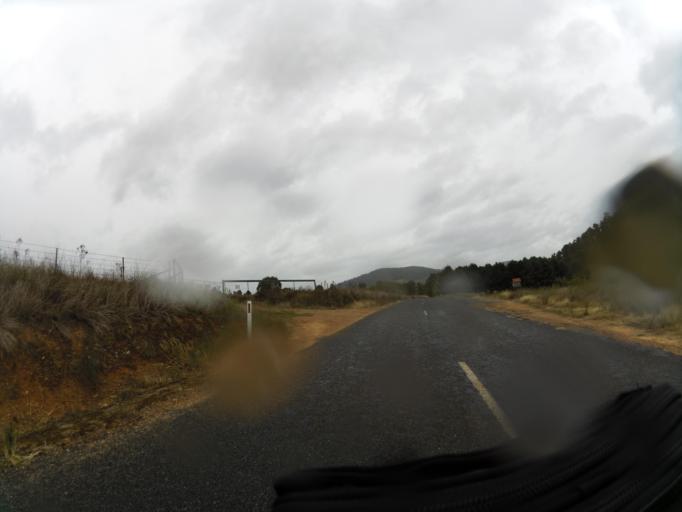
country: AU
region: New South Wales
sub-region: Greater Hume Shire
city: Holbrook
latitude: -36.2308
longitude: 147.6551
